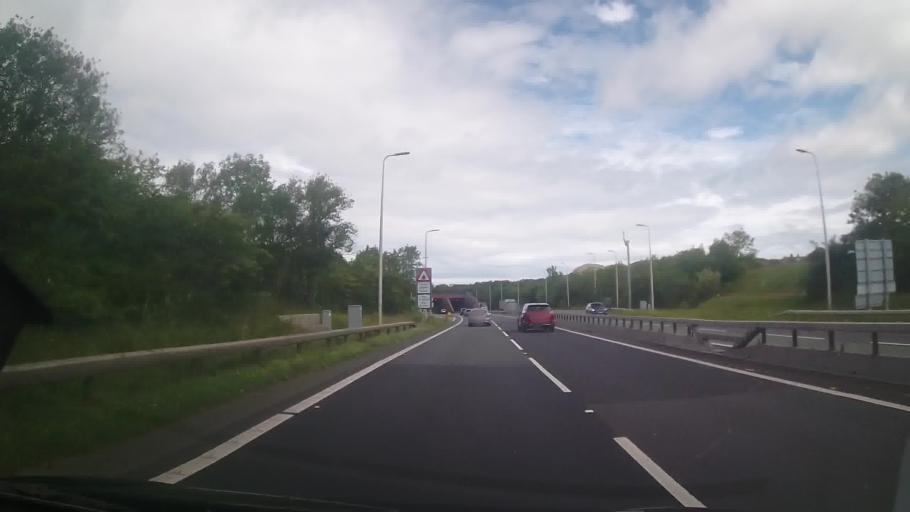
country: GB
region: Wales
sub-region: Conwy
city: Conwy
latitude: 53.2845
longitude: -3.8187
